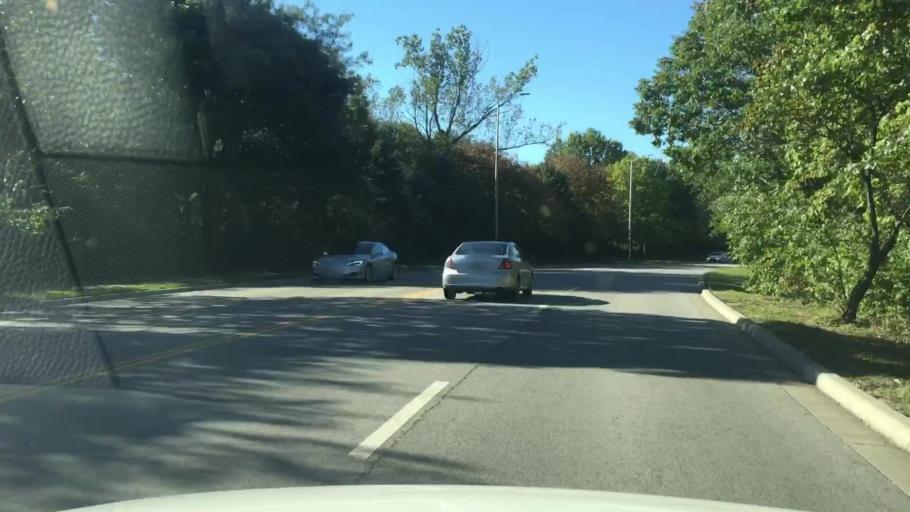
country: US
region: Kansas
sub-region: Johnson County
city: Leawood
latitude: 38.9290
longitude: -94.6275
